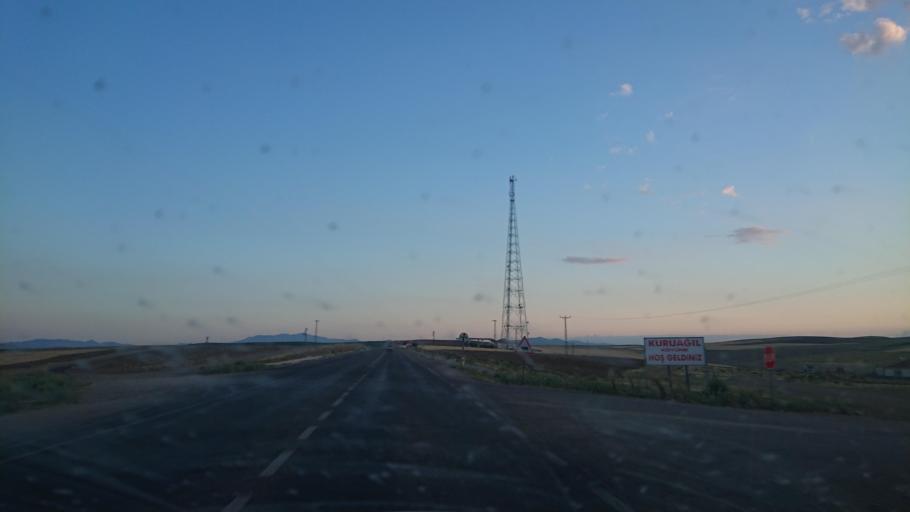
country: TR
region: Kirsehir
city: Kirsehir
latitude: 38.9320
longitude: 34.1839
